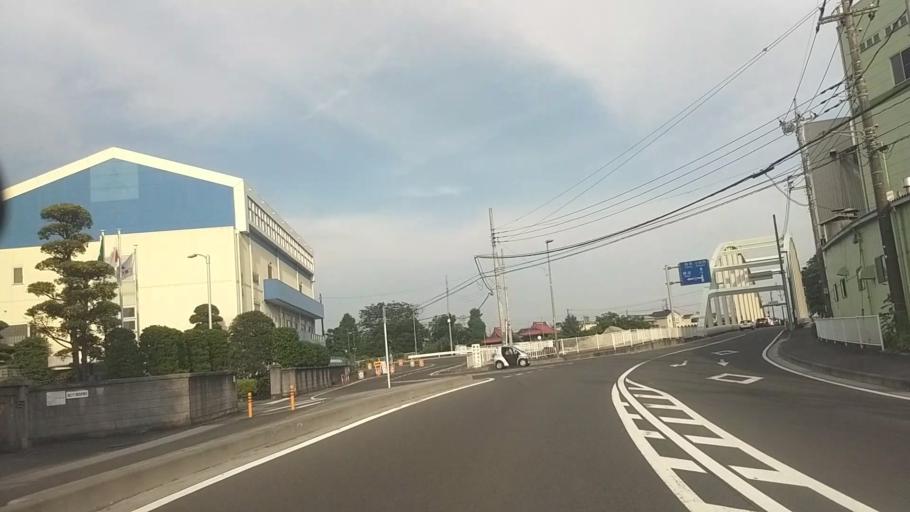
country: JP
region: Kanagawa
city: Odawara
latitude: 35.3480
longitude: 139.0960
